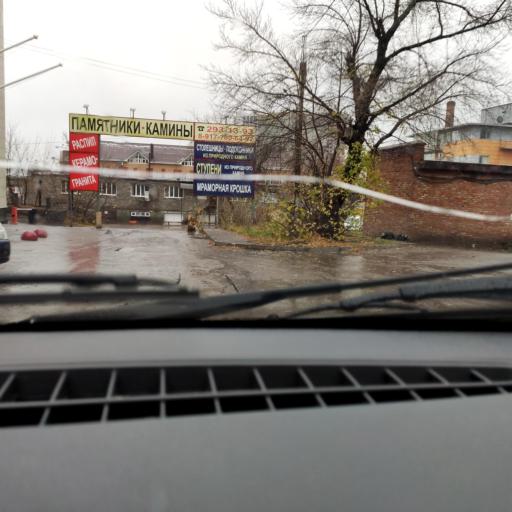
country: RU
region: Bashkortostan
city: Ufa
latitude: 54.7291
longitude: 55.9860
